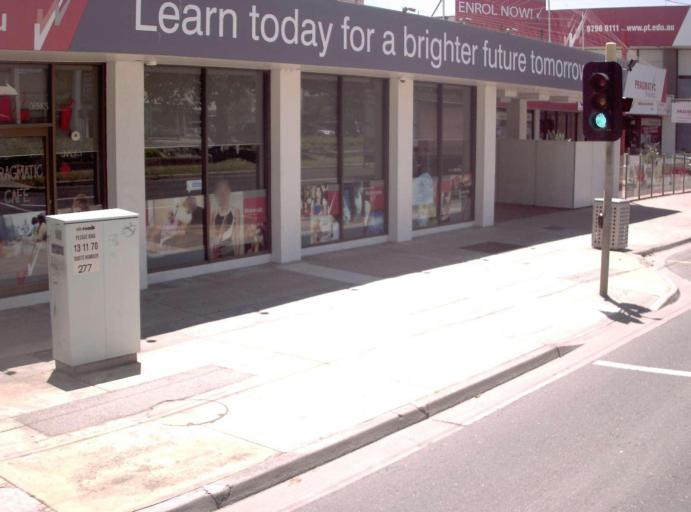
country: AU
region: Victoria
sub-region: Frankston
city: Frankston
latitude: -38.1419
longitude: 145.1214
